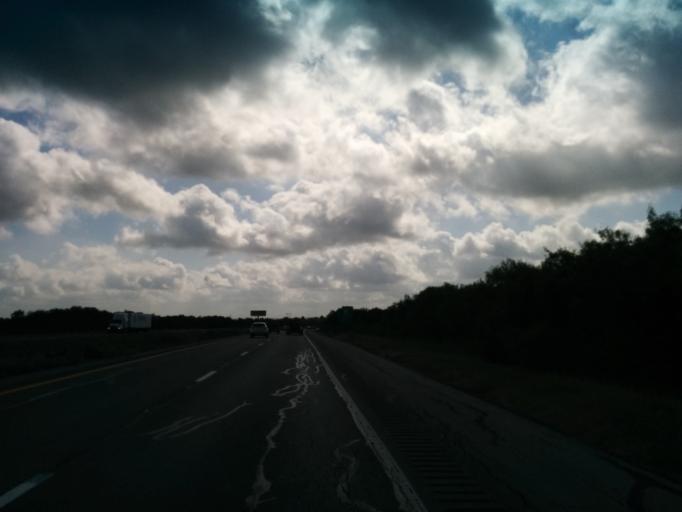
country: US
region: Texas
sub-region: Caldwell County
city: Luling
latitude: 29.6507
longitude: -97.6759
